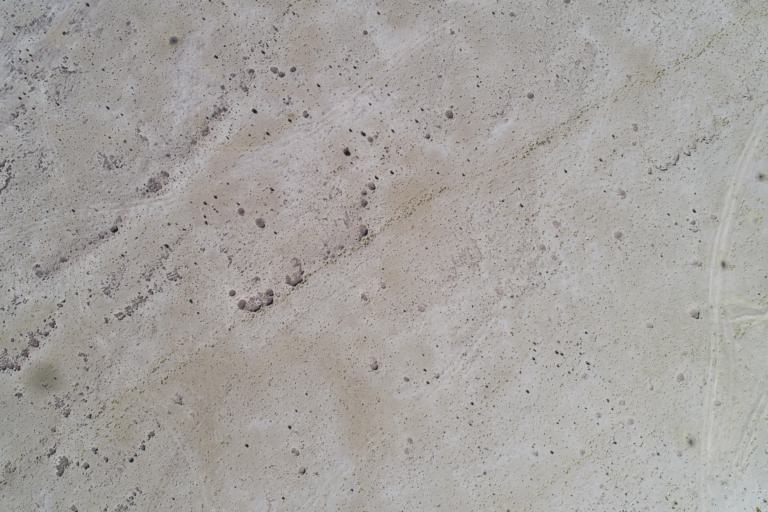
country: BO
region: Potosi
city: Colchani
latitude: -20.3505
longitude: -66.9042
